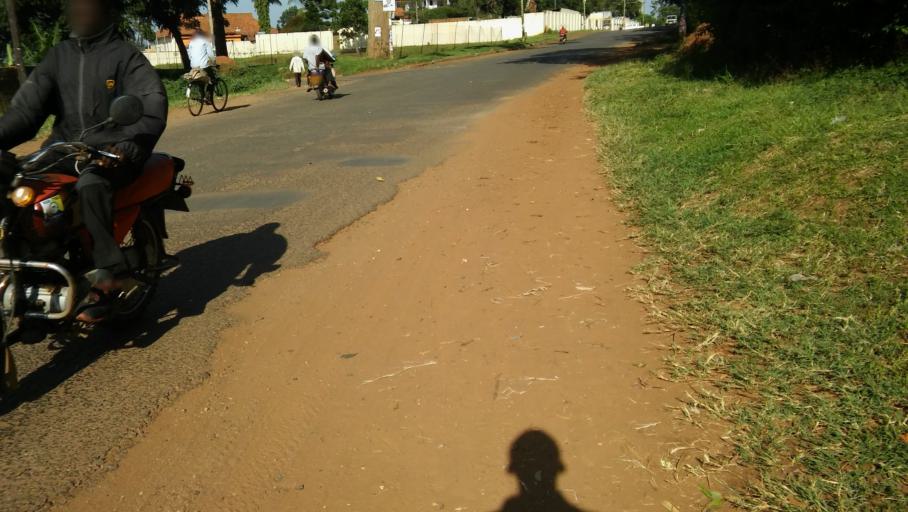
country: UG
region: Eastern Region
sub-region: Mbale District
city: Mbale
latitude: 1.0682
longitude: 34.1870
